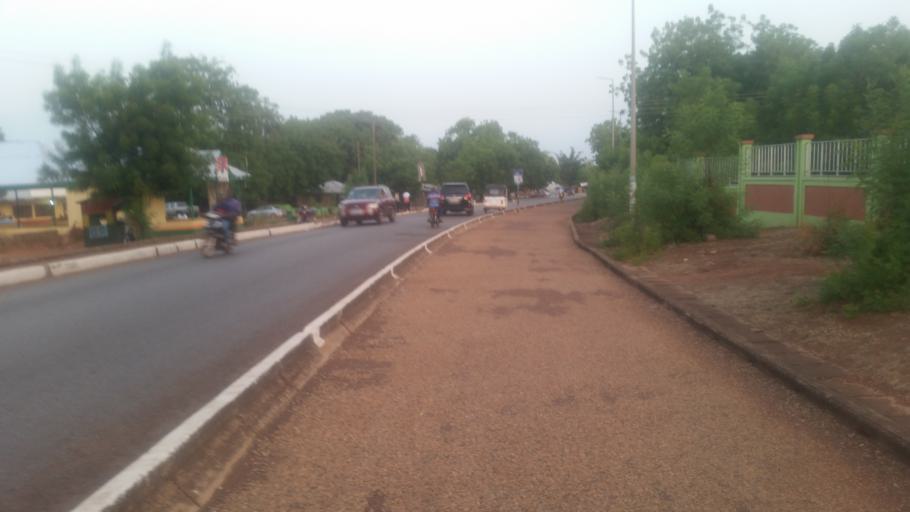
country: GH
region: Northern
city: Tamale
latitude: 9.4061
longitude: -0.8315
